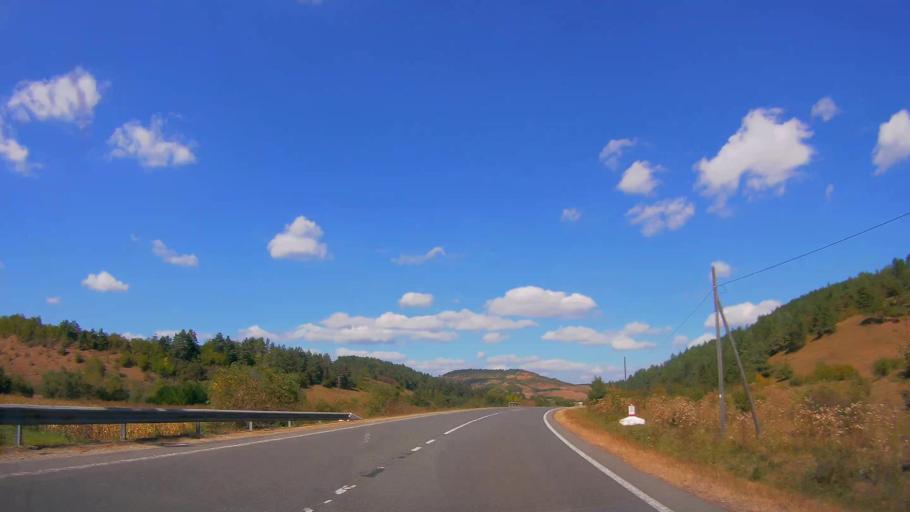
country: RO
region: Cluj
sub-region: Comuna Sanpaul
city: Sanpaul
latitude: 46.8431
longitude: 23.4044
